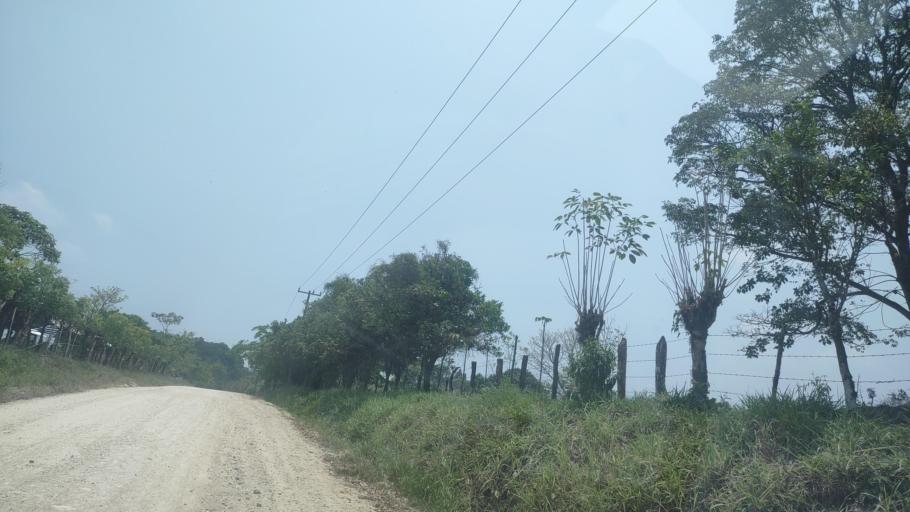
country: MX
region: Chiapas
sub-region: Tecpatan
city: Raudales Malpaso
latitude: 17.4615
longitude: -93.8058
